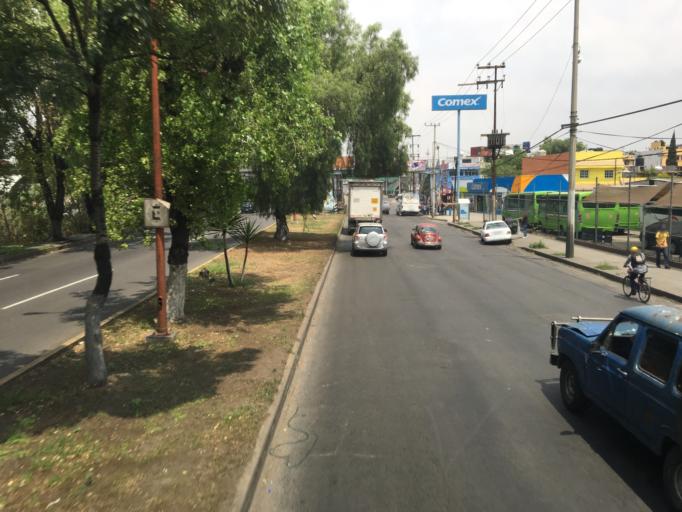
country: MX
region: Mexico
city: Tlalnepantla
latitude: 19.5323
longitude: -99.1786
